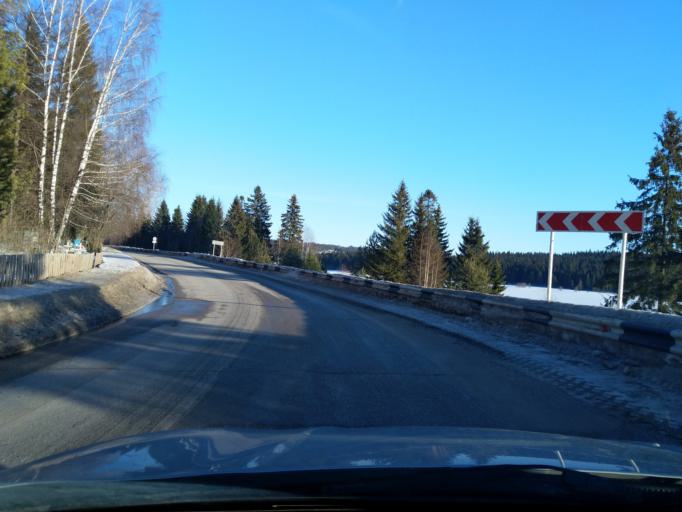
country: RU
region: Perm
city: Polazna
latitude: 58.3043
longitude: 56.4302
